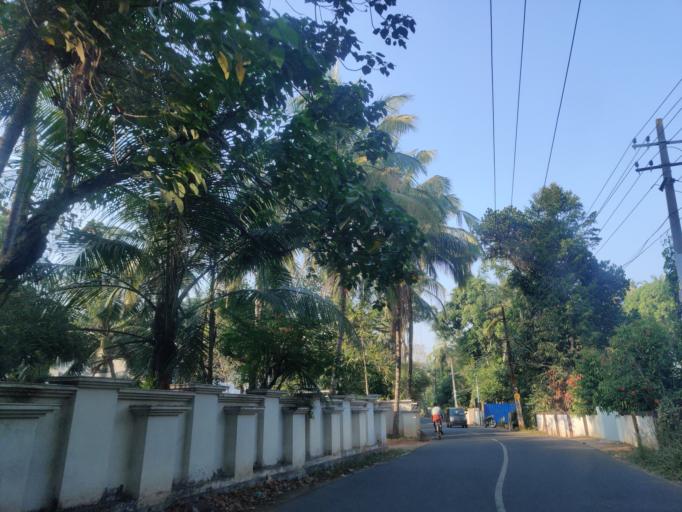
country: IN
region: Kerala
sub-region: Malappuram
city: Ponnani
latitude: 10.7301
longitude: 76.0126
